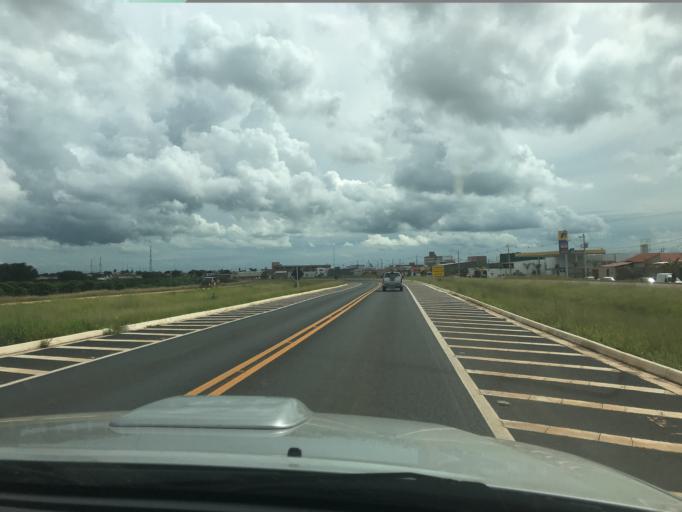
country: BR
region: Minas Gerais
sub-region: Patrocinio
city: Patrocinio
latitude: -19.0985
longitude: -46.6746
